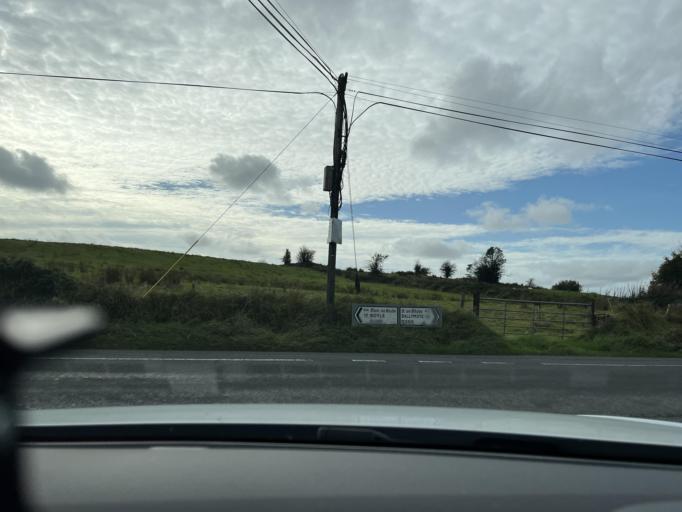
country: IE
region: Connaught
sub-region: Roscommon
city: Boyle
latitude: 54.0237
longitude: -8.4018
